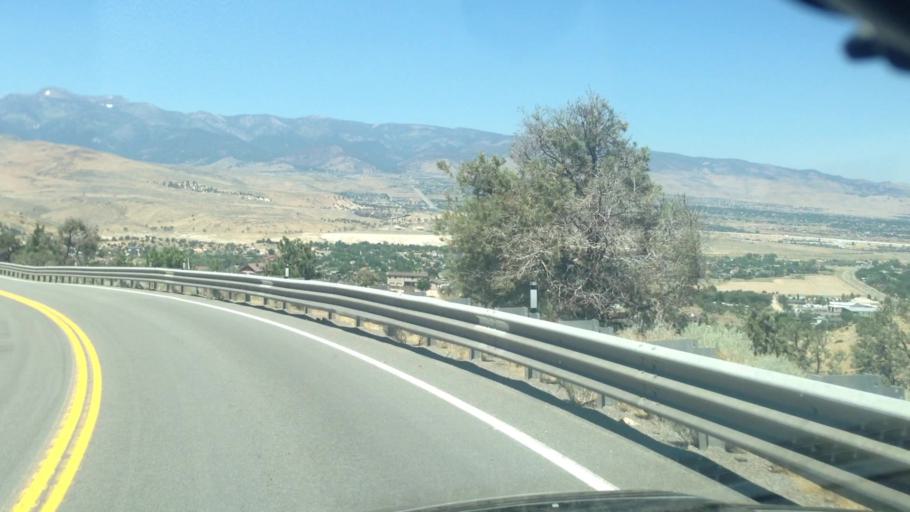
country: US
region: Nevada
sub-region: Storey County
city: Virginia City
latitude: 39.3865
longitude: -119.7098
